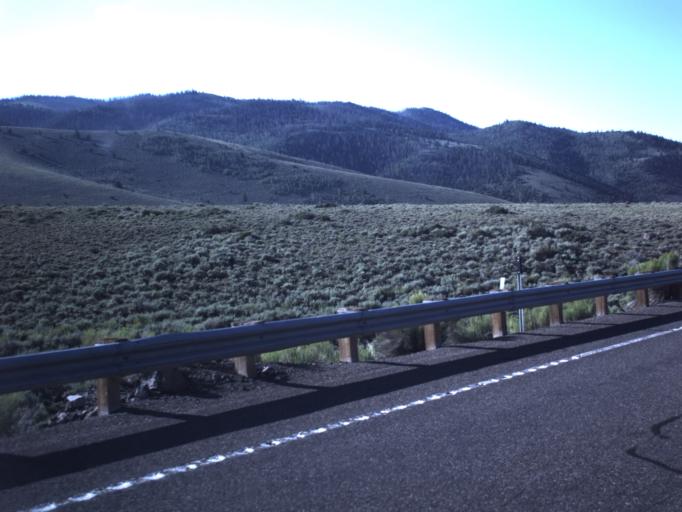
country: US
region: Utah
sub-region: Wayne County
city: Loa
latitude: 38.5477
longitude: -111.5104
